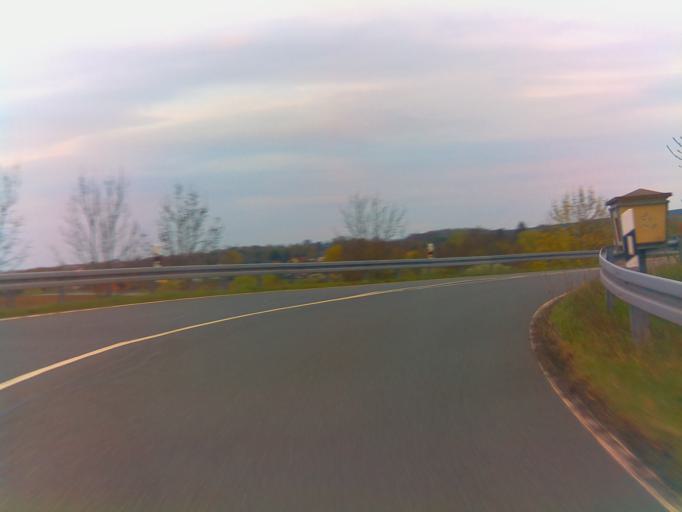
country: DE
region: Thuringia
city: Neustadt (Orla)
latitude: 50.7325
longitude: 11.7220
